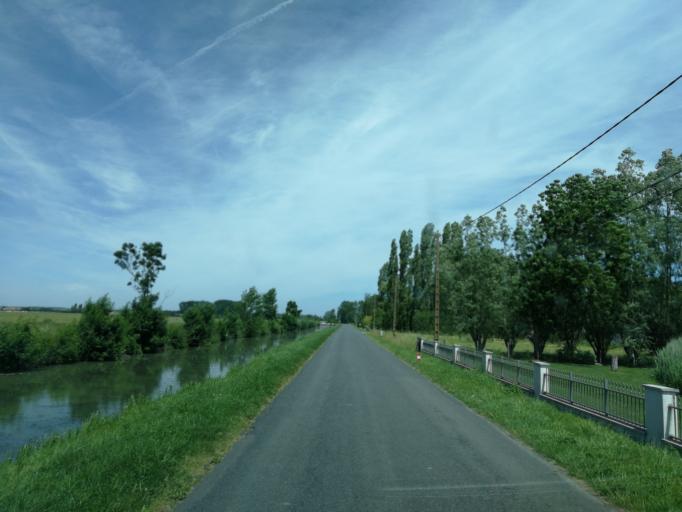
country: FR
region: Pays de la Loire
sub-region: Departement de la Vendee
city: Le Langon
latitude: 46.4131
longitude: -0.9201
